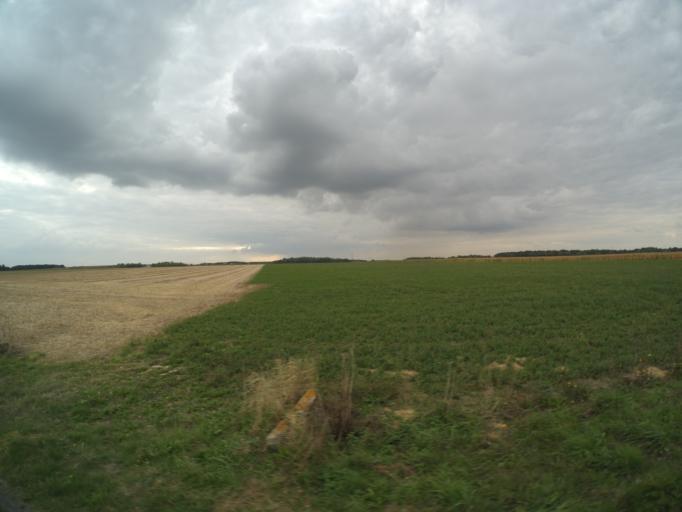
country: FR
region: Centre
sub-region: Departement d'Indre-et-Loire
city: Auzouer-en-Touraine
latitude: 47.4965
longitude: 0.9474
